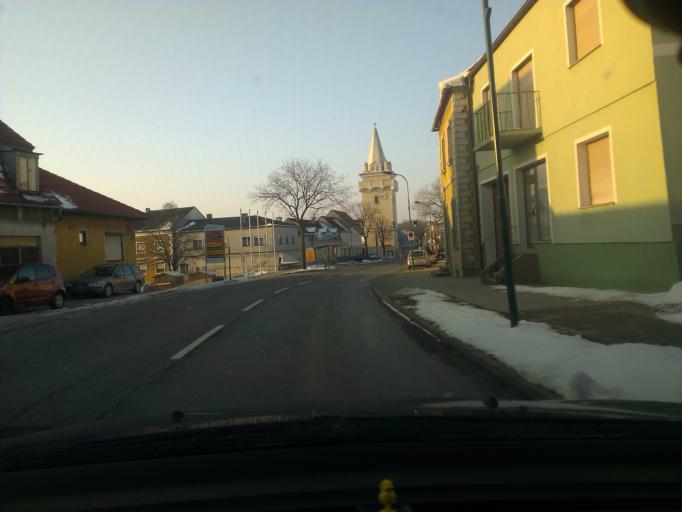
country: AT
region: Burgenland
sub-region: Eisenstadt-Umgebung
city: Breitenbrunn
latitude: 47.9466
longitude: 16.7338
